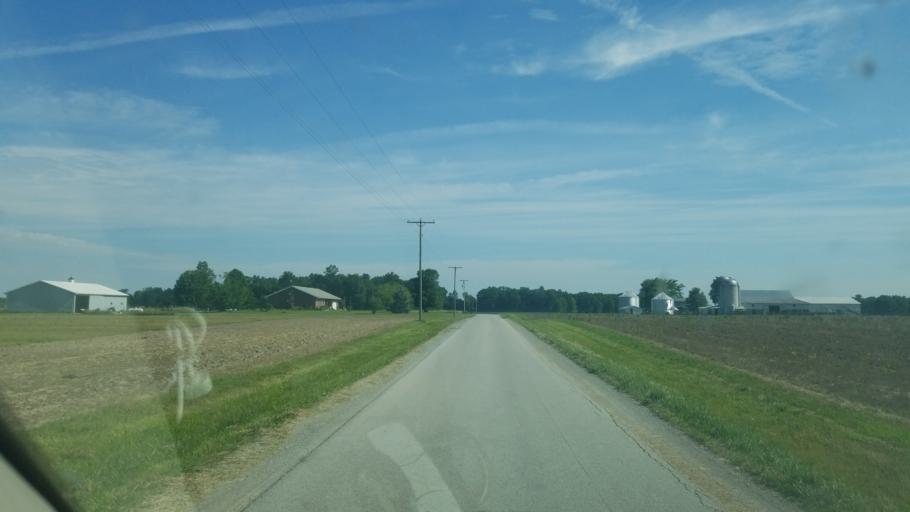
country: US
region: Ohio
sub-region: Wyandot County
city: Upper Sandusky
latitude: 40.8624
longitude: -83.2371
